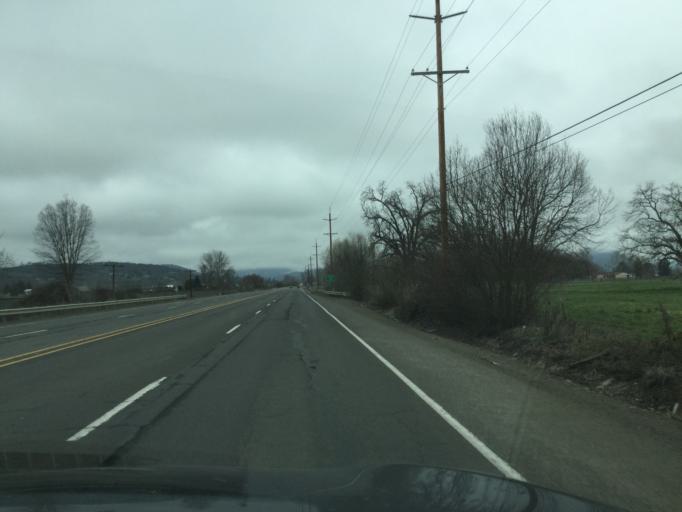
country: US
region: Oregon
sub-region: Jackson County
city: Central Point
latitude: 42.3926
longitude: -122.9363
